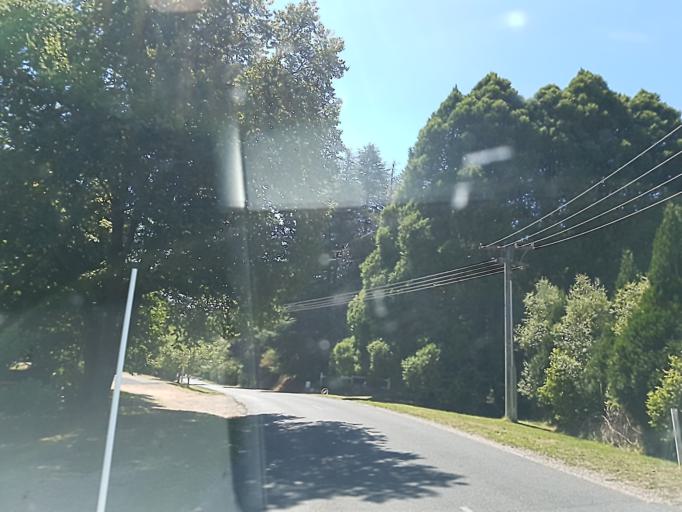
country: AU
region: Victoria
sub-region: Alpine
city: Mount Beauty
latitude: -36.7781
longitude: 146.9831
